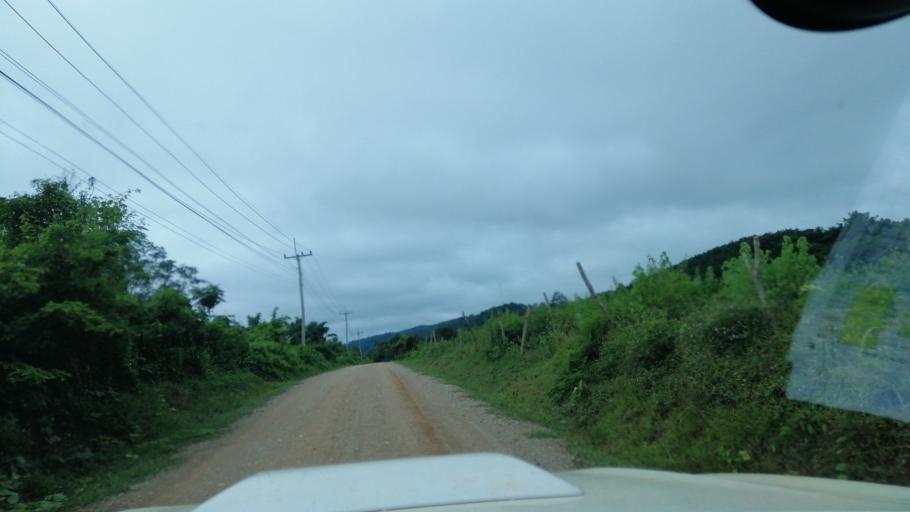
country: LA
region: Xiagnabouli
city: Muang Kenthao
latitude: 17.9582
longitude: 101.4084
